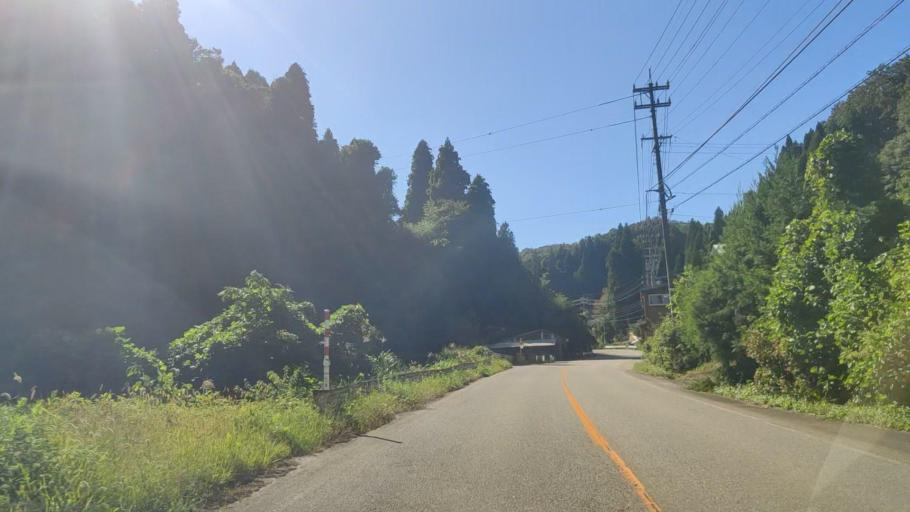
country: JP
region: Ishikawa
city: Nanao
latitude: 37.3218
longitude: 137.1809
